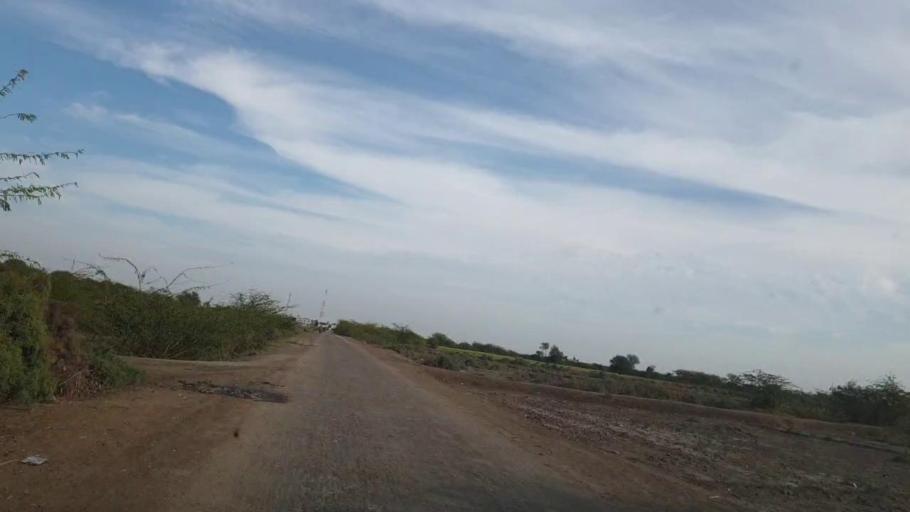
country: PK
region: Sindh
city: Pithoro
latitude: 25.6292
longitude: 69.4110
